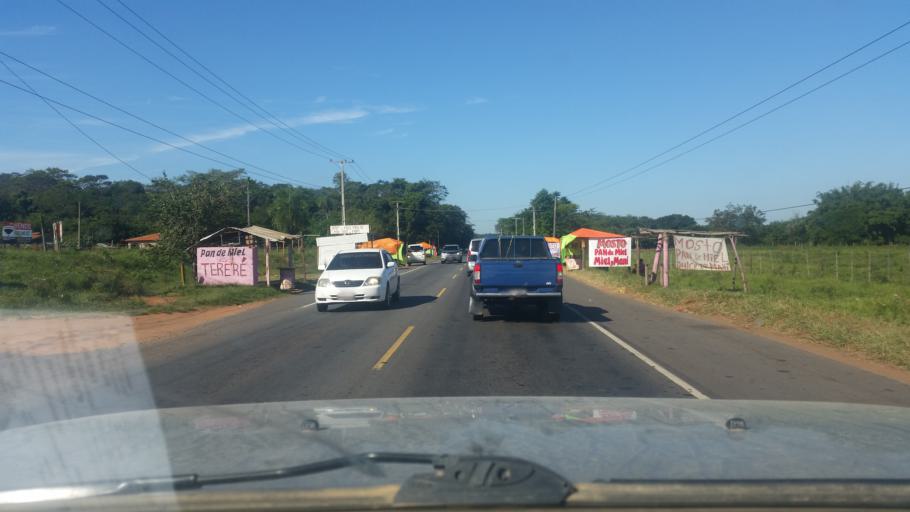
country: PY
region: Central
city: Ita
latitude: -25.5220
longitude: -57.3725
